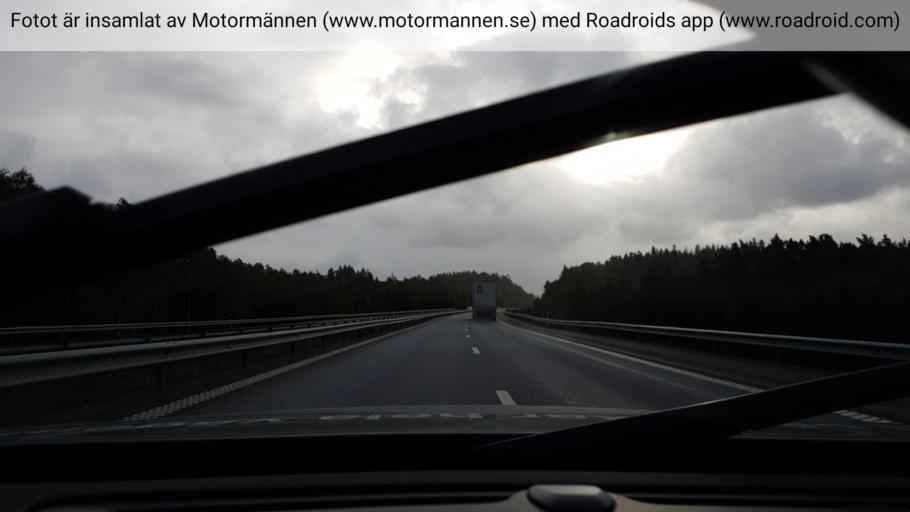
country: SE
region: Vaestra Goetaland
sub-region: Harryda Kommun
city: Ravlanda
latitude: 57.6719
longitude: 12.5107
